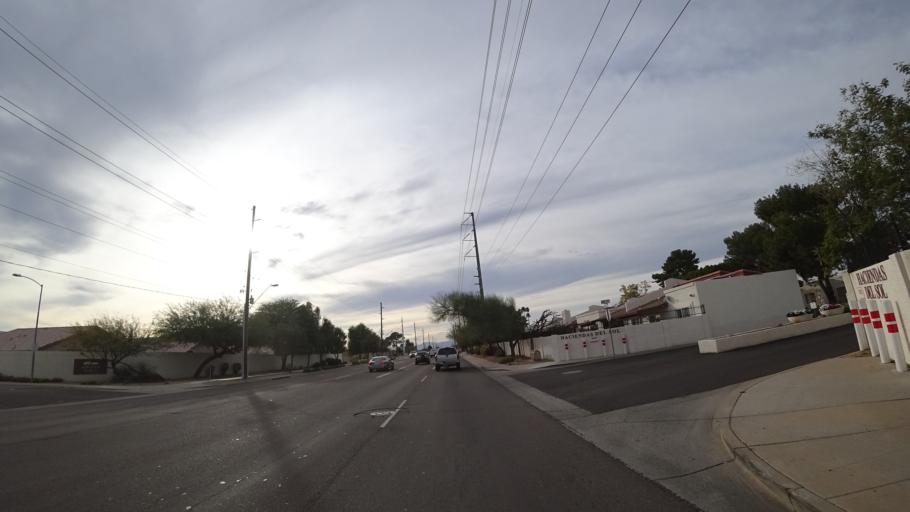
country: US
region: Arizona
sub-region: Maricopa County
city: Peoria
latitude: 33.5672
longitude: -112.2059
